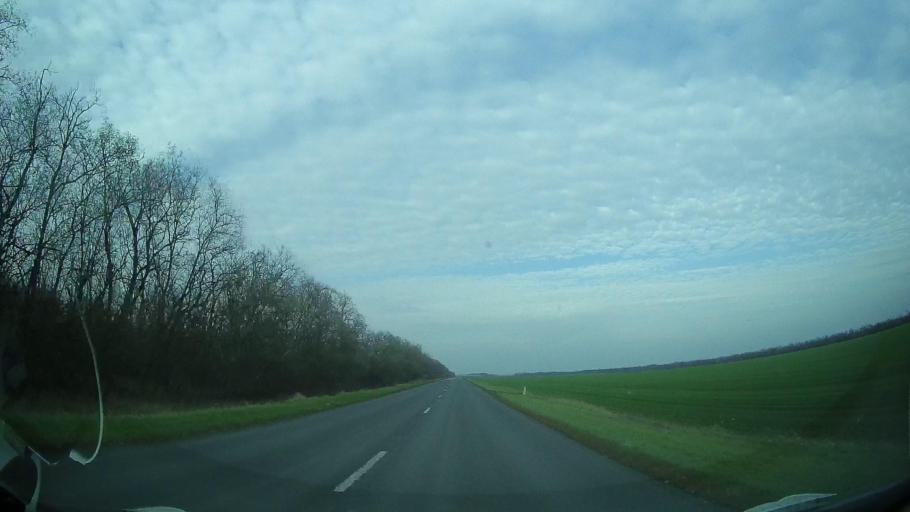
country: RU
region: Rostov
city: Zernograd
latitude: 46.9493
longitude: 40.3667
